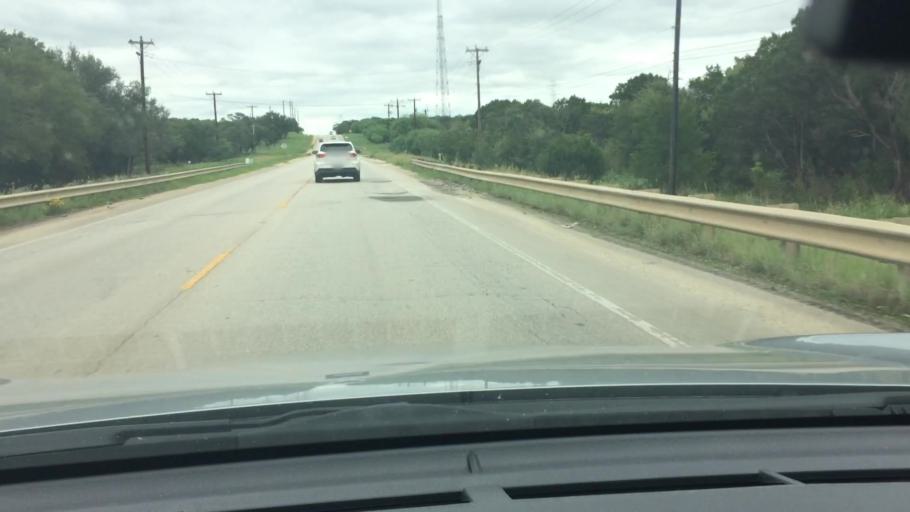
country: US
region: Texas
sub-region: Comal County
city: Garden Ridge
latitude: 29.6450
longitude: -98.3968
